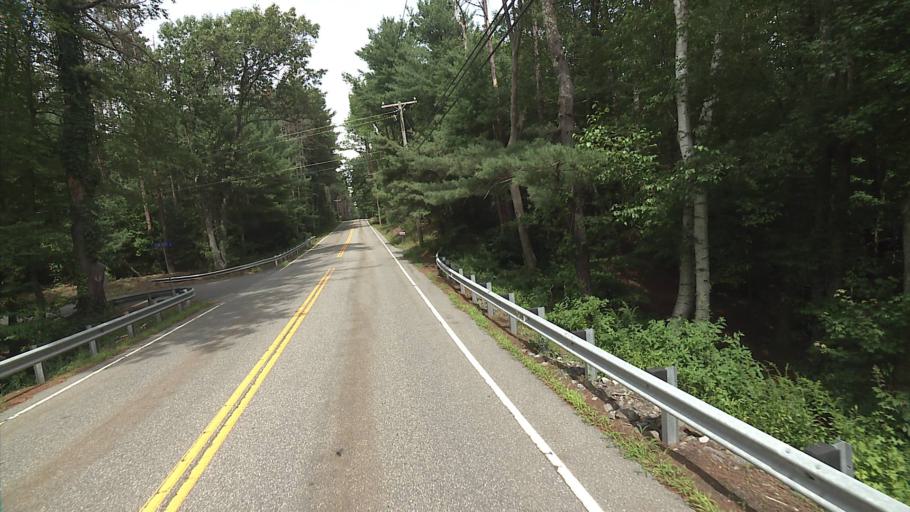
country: US
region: Massachusetts
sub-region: Hampden County
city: Holland
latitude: 42.0063
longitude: -72.1482
